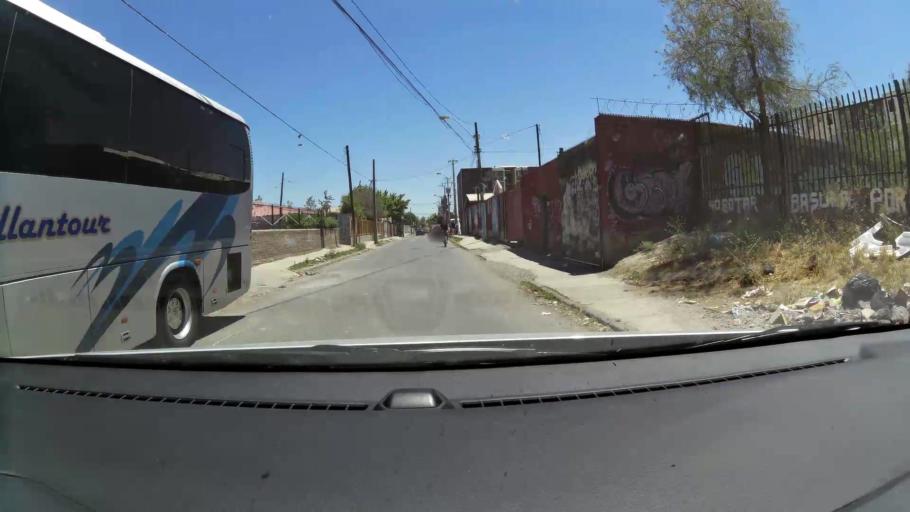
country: CL
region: Santiago Metropolitan
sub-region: Provincia de Santiago
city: La Pintana
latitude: -33.5795
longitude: -70.6680
